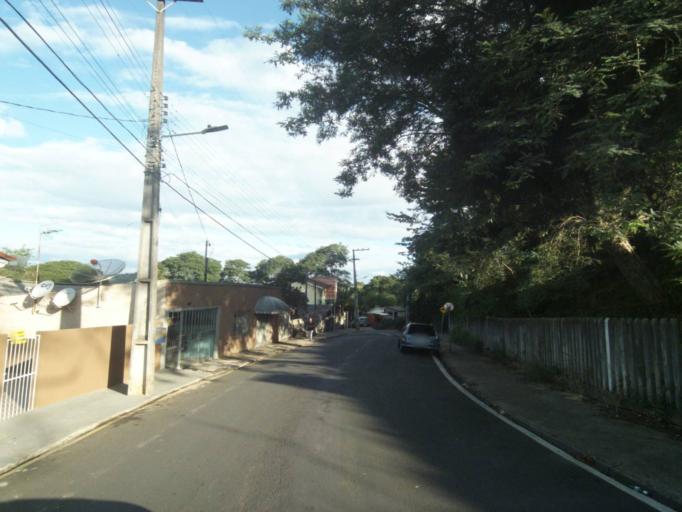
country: BR
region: Parana
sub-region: Telemaco Borba
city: Telemaco Borba
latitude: -24.3254
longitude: -50.6137
